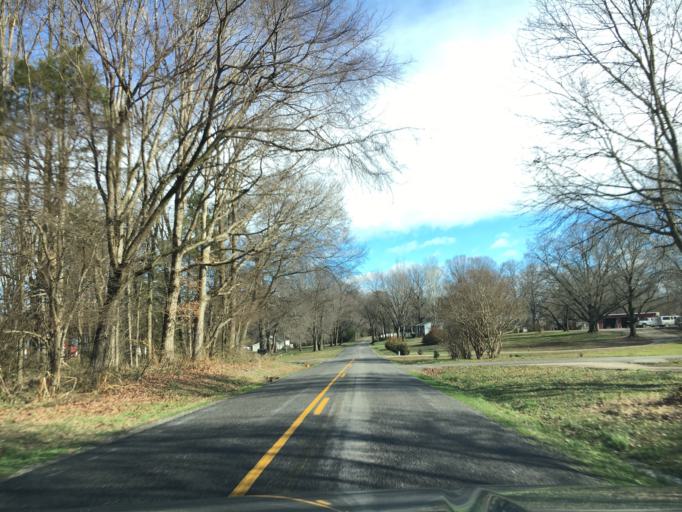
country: US
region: Virginia
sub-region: Amelia County
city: Amelia Court House
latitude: 37.4405
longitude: -78.0197
